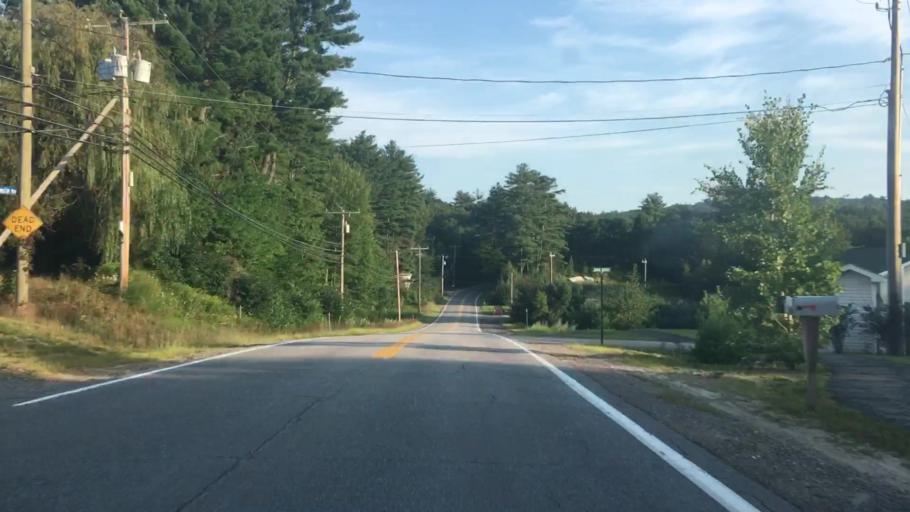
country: US
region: New Hampshire
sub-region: Belknap County
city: Laconia
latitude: 43.5086
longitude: -71.4506
